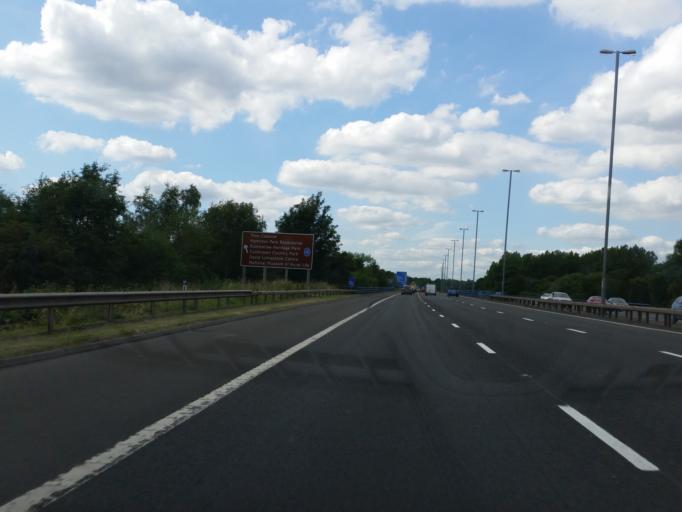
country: GB
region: Scotland
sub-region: South Lanarkshire
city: Bothwell
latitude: 55.7953
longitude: -4.0450
